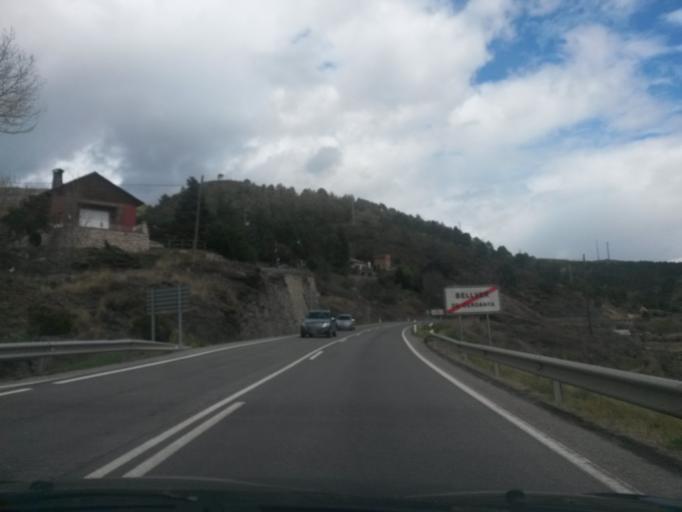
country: ES
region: Catalonia
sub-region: Provincia de Lleida
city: Bellver de Cerdanya
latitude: 42.3740
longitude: 1.7761
